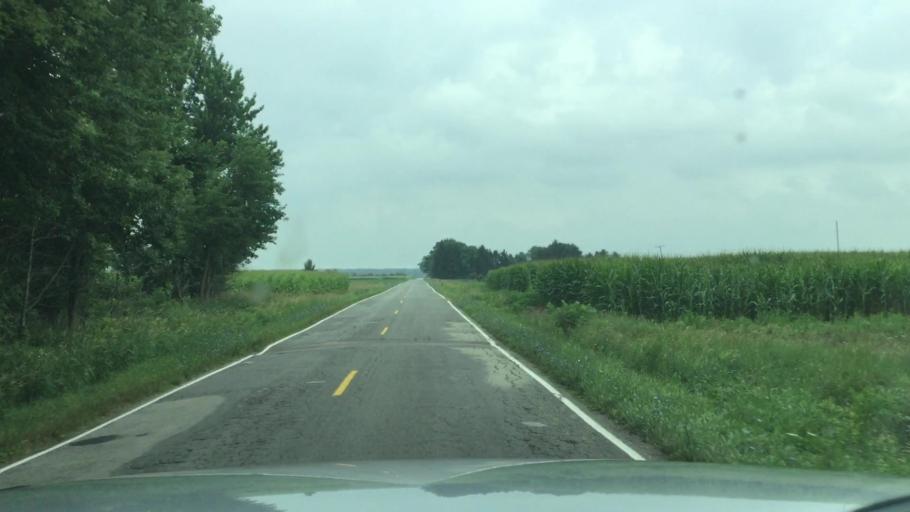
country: US
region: Michigan
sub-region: Shiawassee County
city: New Haven
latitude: 43.0767
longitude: -84.2261
